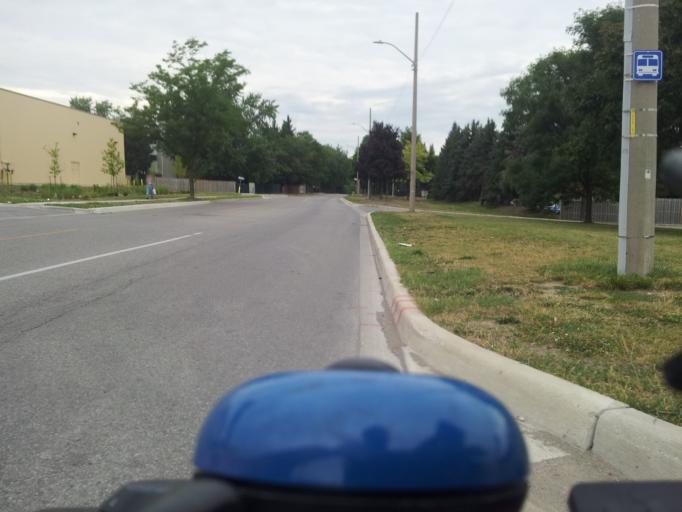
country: CA
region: Ontario
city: Stratford
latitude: 43.3715
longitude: -80.9482
